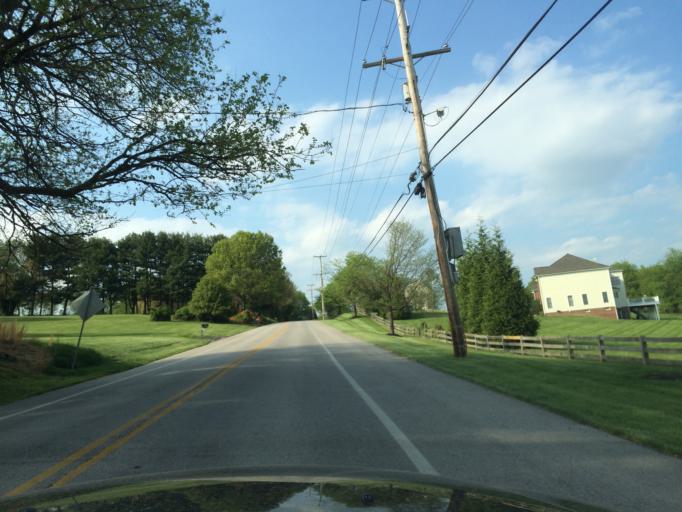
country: US
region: Maryland
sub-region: Howard County
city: Highland
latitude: 39.2079
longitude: -76.9799
